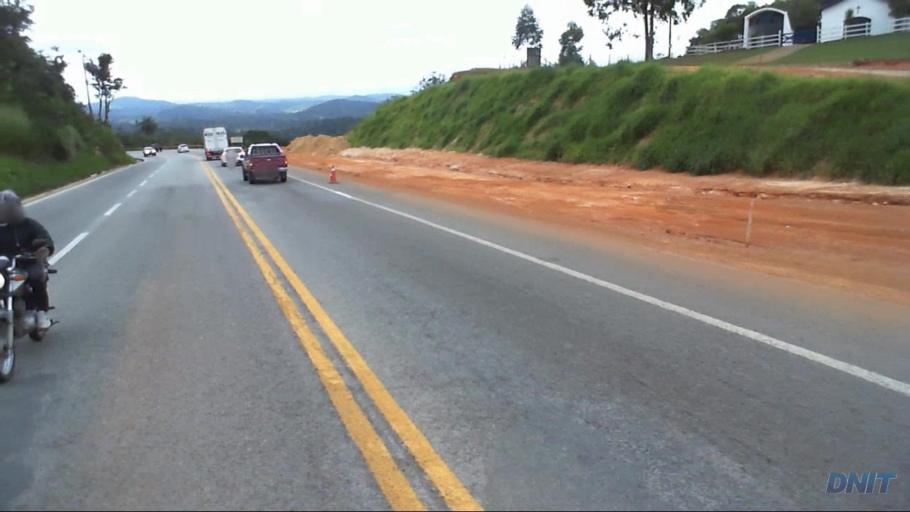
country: BR
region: Minas Gerais
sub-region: Caete
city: Caete
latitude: -19.7487
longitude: -43.5223
